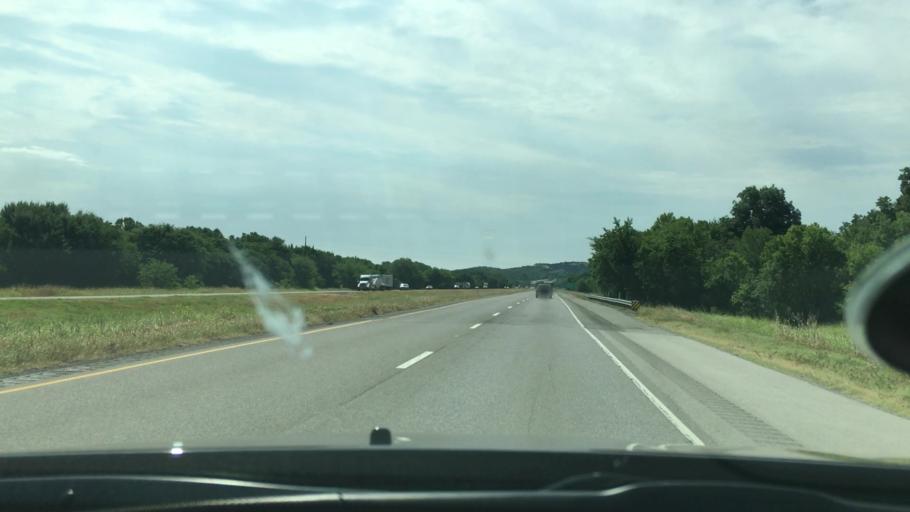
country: US
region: Oklahoma
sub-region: Murray County
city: Davis
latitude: 34.4646
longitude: -97.1490
